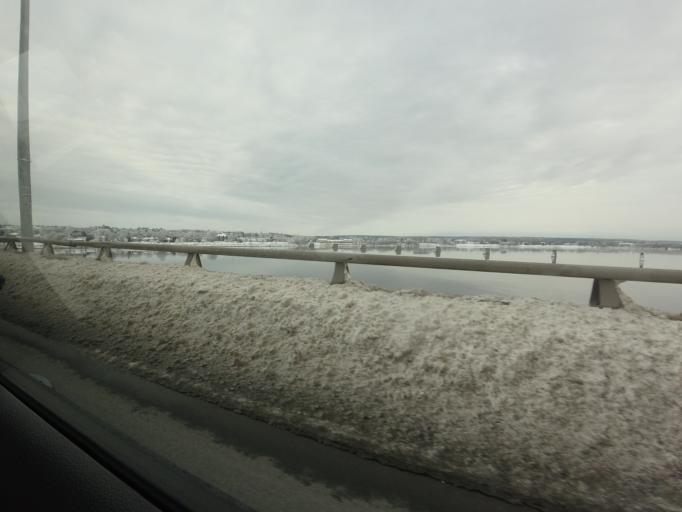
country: CA
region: New Brunswick
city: Fredericton
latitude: 45.9664
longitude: -66.6435
